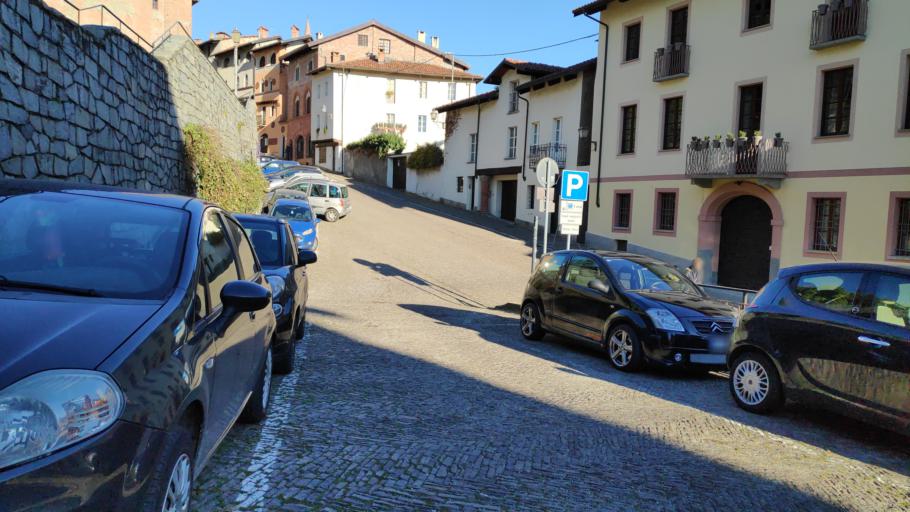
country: IT
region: Piedmont
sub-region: Provincia di Torino
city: Pinerolo
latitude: 44.8858
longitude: 7.3280
